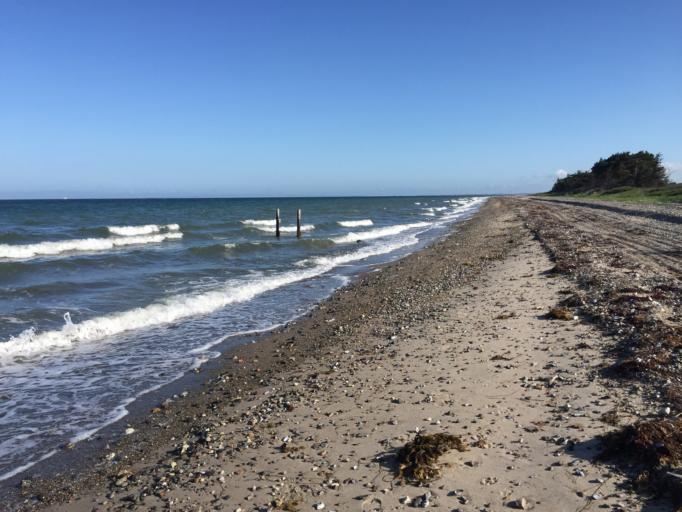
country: DK
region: Zealand
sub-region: Slagelse Kommune
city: Korsor
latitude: 55.2105
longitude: 11.1728
